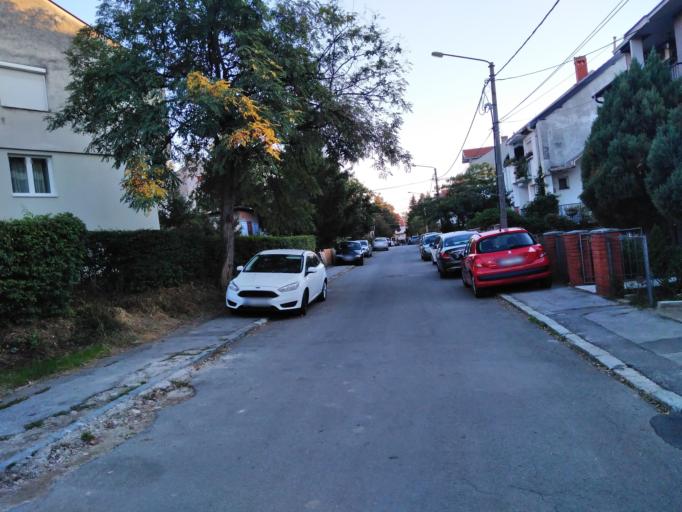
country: RS
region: Central Serbia
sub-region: Belgrade
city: Rakovica
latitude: 44.7519
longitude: 20.4211
